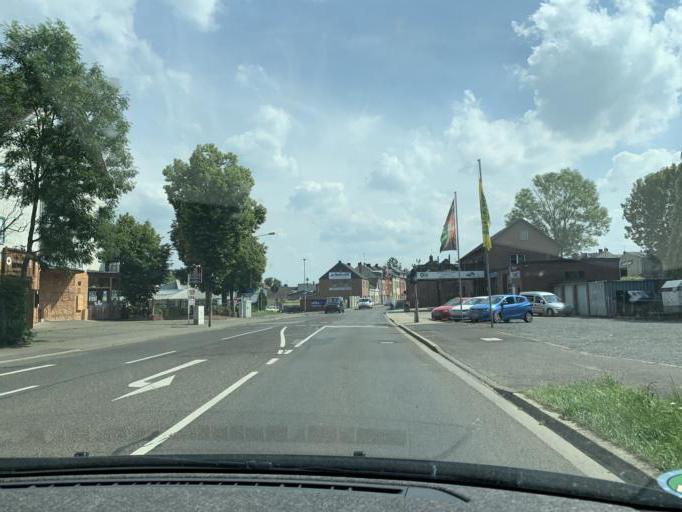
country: DE
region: North Rhine-Westphalia
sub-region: Regierungsbezirk Koln
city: Bedburg
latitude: 50.9950
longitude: 6.5698
